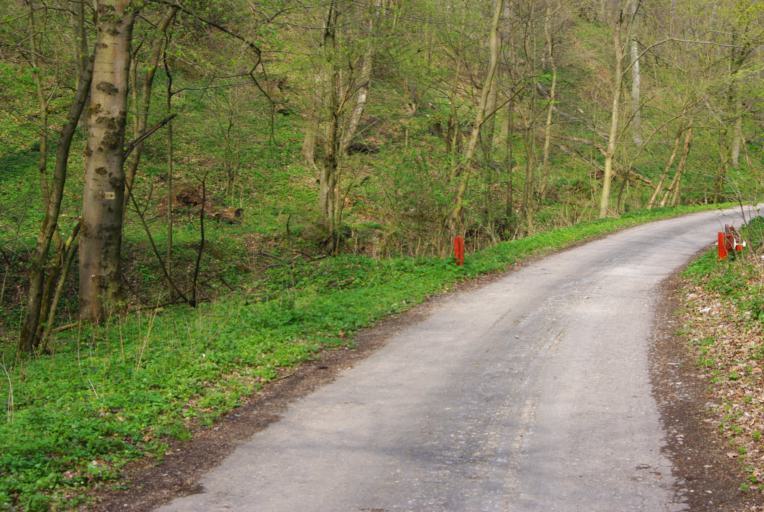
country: HU
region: Fejer
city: Szarliget
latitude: 47.4577
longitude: 18.4710
